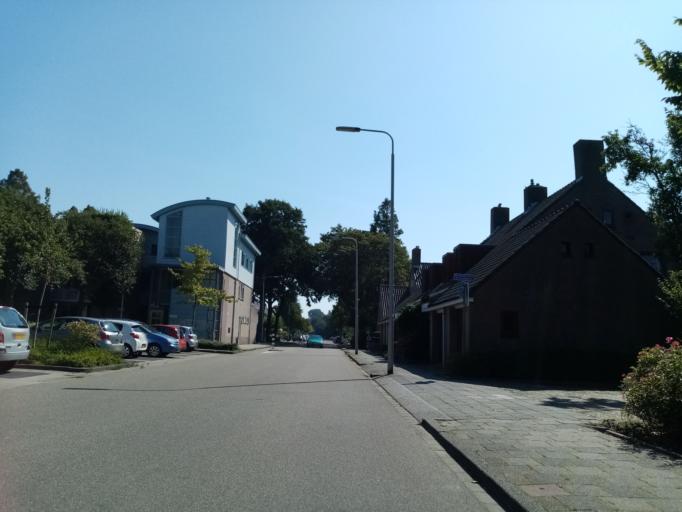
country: NL
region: South Holland
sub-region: Gemeente Lisse
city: Lisse
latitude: 52.2482
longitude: 4.5604
